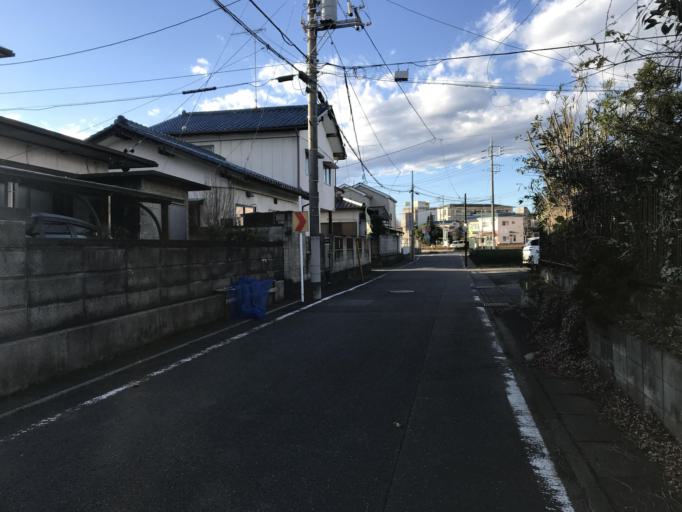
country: JP
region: Ibaraki
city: Naka
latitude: 36.0871
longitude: 140.1921
